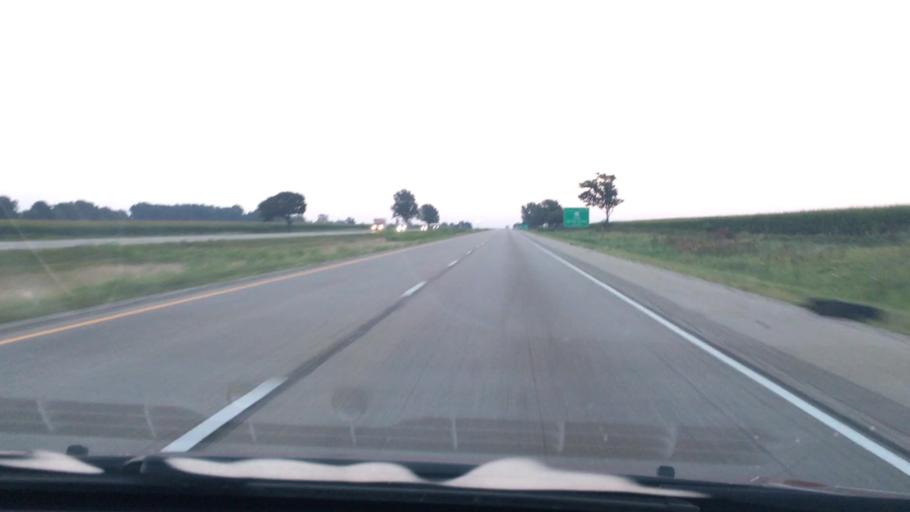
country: US
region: Illinois
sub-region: Bureau County
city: Ladd
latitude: 41.3703
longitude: -89.2344
